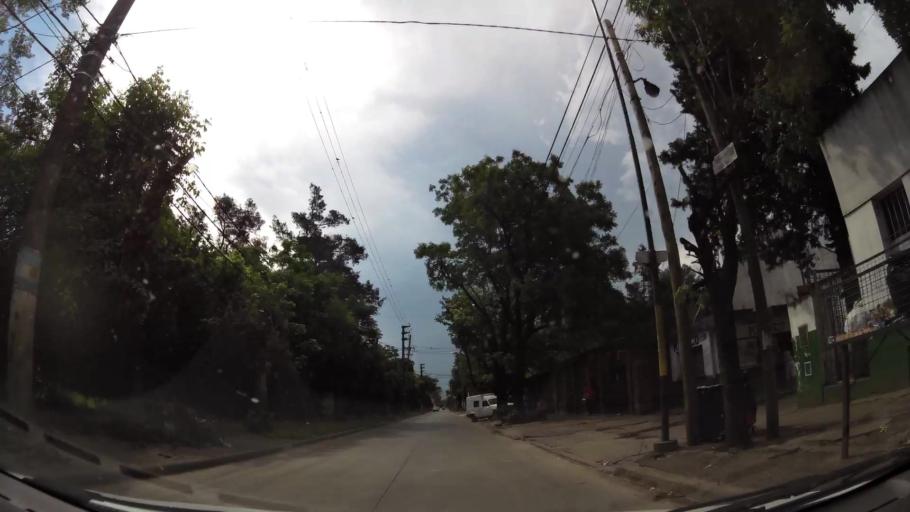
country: AR
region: Buenos Aires
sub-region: Partido de Merlo
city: Merlo
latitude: -34.6306
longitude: -58.7015
